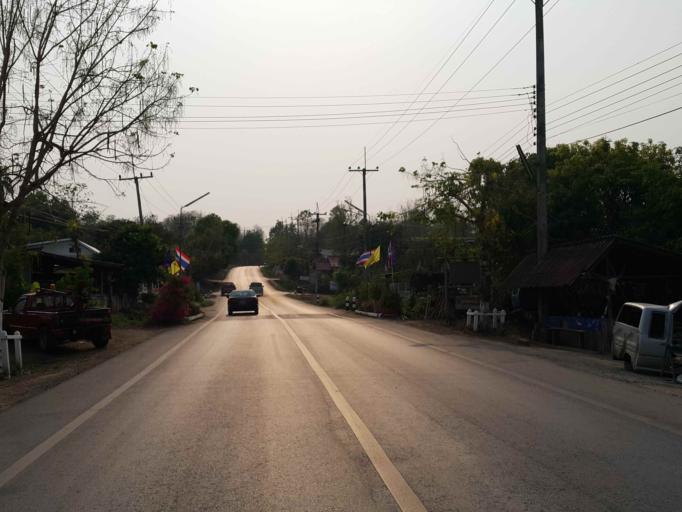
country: TH
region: Chiang Mai
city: Mae Taeng
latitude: 19.1439
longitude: 98.9841
